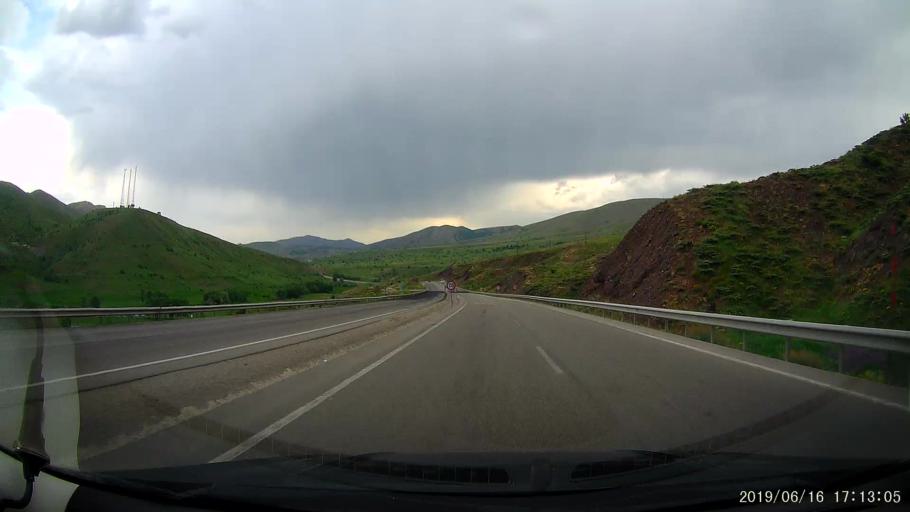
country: TR
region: Erzurum
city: Askale
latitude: 39.8602
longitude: 40.6058
